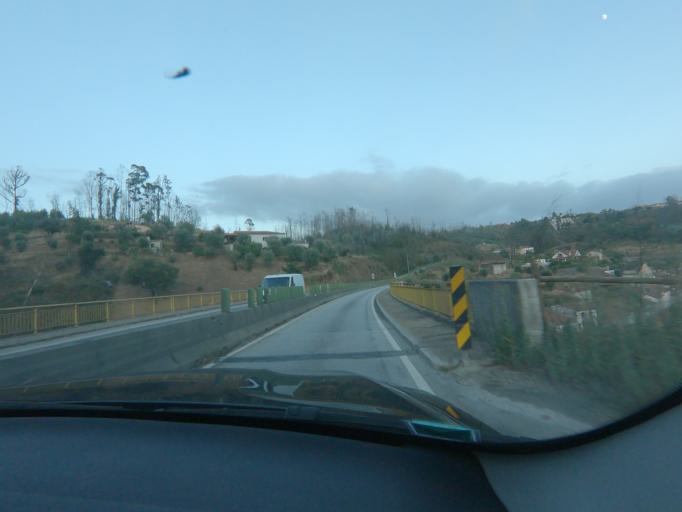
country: PT
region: Coimbra
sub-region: Penacova
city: Penacova
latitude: 40.3065
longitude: -8.2304
